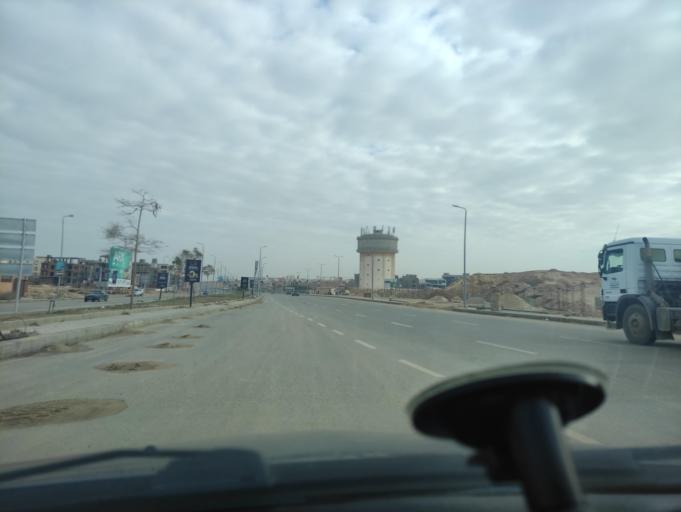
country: EG
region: Muhafazat al Qalyubiyah
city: Al Khankah
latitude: 30.0438
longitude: 31.5242
